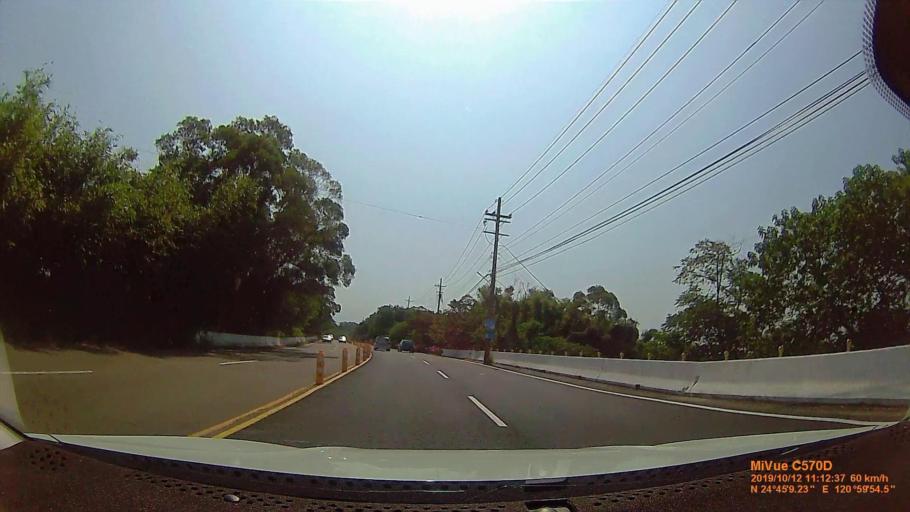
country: TW
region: Taiwan
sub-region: Hsinchu
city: Hsinchu
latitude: 24.7524
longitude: 120.9985
